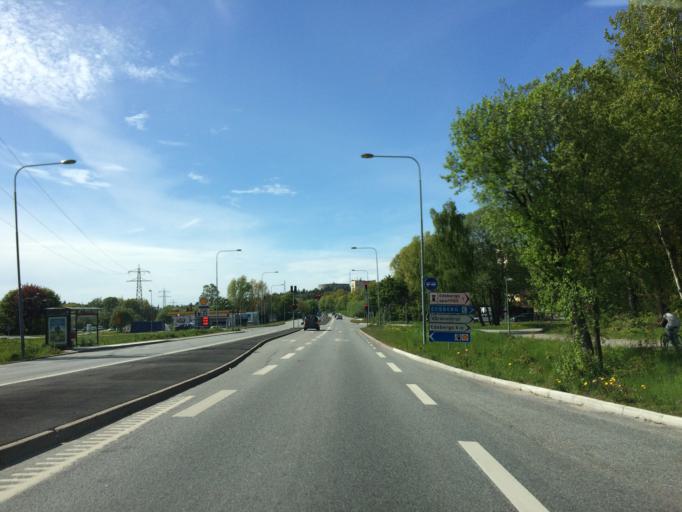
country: SE
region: Stockholm
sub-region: Sollentuna Kommun
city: Sollentuna
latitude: 59.4430
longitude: 17.9675
